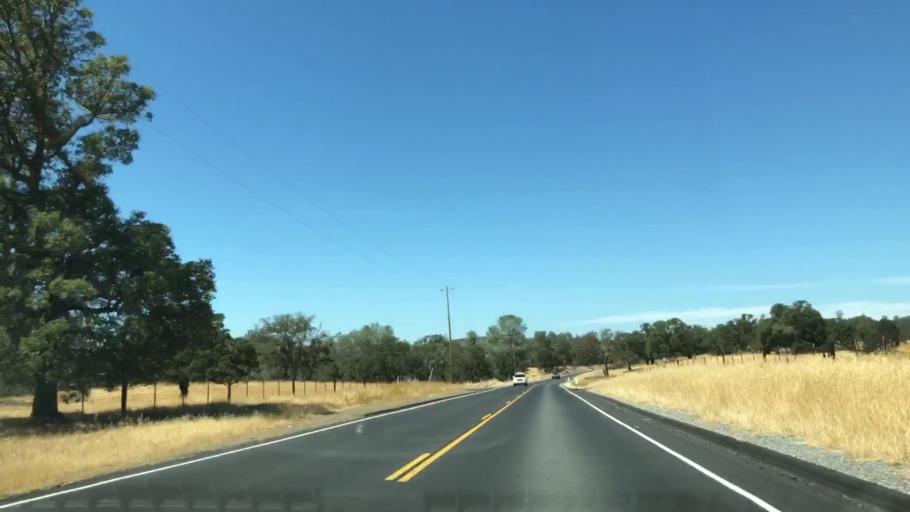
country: US
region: California
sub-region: Calaveras County
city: Copperopolis
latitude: 37.9695
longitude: -120.6253
